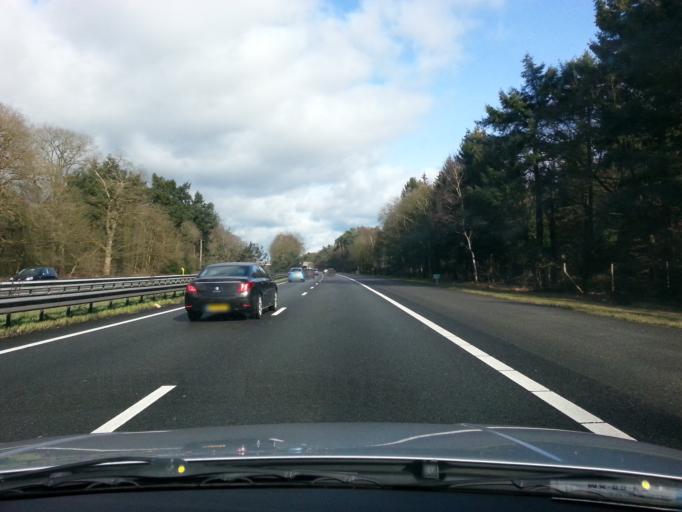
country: NL
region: Gelderland
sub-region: Gemeente Nunspeet
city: Nunspeet
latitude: 52.3437
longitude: 5.7077
